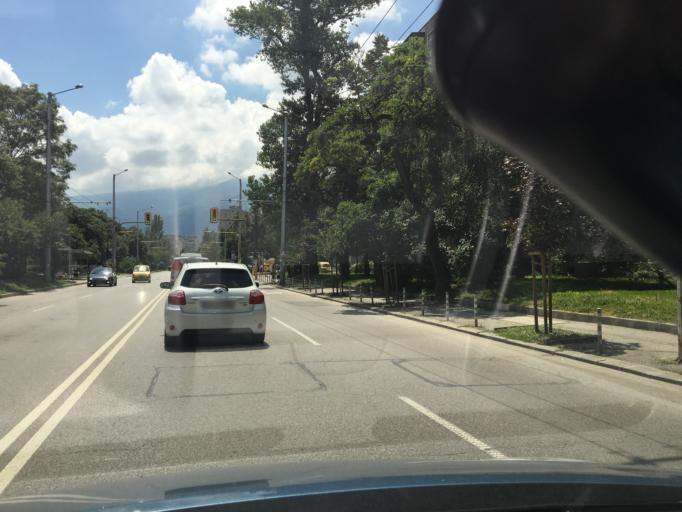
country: BG
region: Sofia-Capital
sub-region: Stolichna Obshtina
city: Sofia
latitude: 42.6705
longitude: 23.3039
